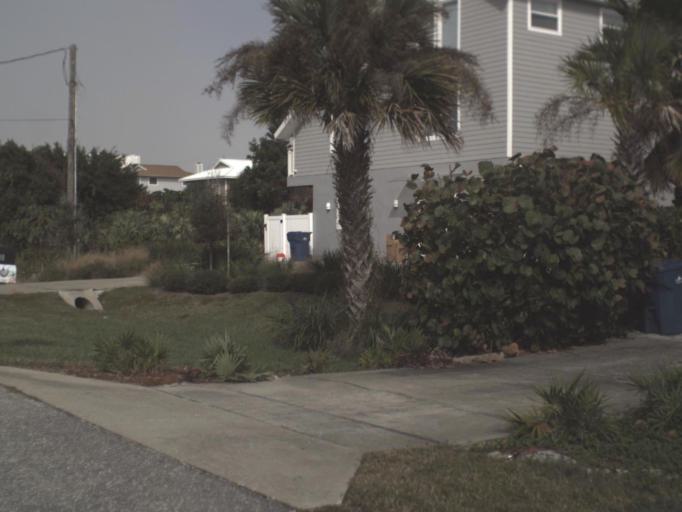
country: US
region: Florida
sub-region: Volusia County
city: Edgewater
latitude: 28.9555
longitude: -80.8434
